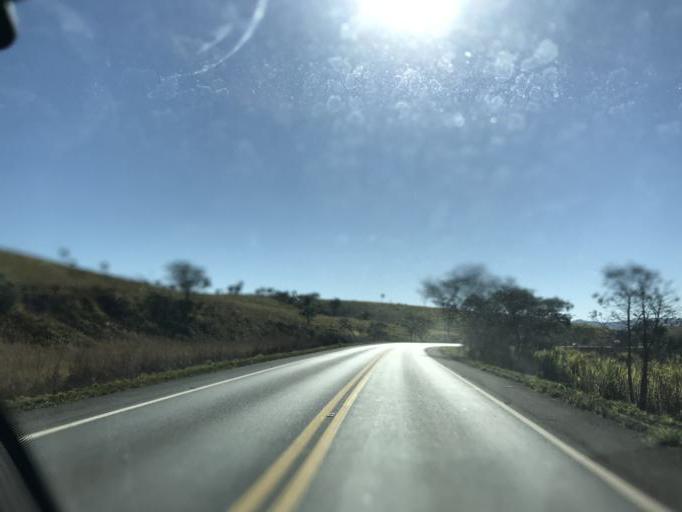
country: BR
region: Minas Gerais
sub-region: Bambui
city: Bambui
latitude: -19.8390
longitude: -46.0013
